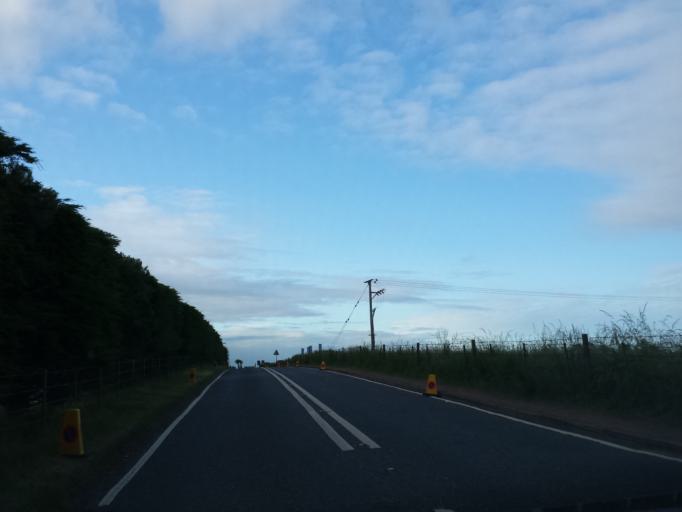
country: GB
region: Scotland
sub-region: Fife
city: Saint Andrews
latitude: 56.3228
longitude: -2.8135
